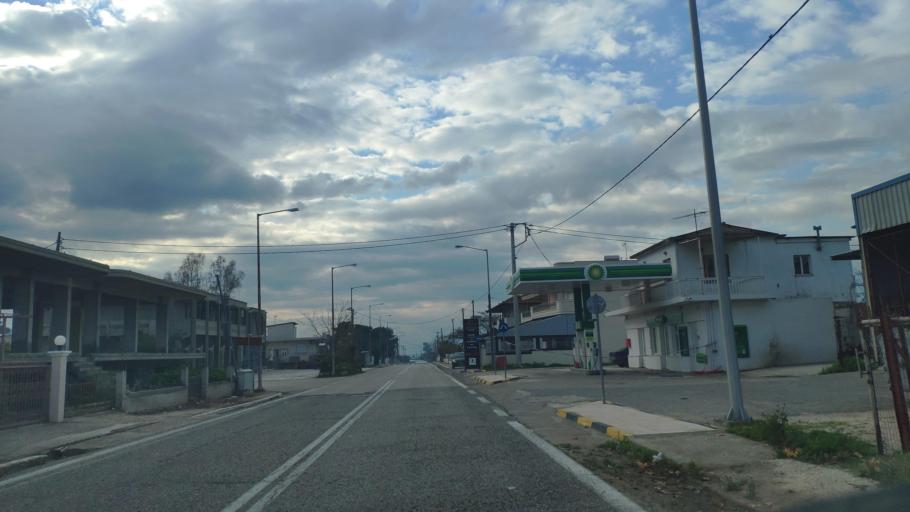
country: GR
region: Peloponnese
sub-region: Nomos Argolidos
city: Koutsopodi
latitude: 37.7205
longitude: 22.7248
